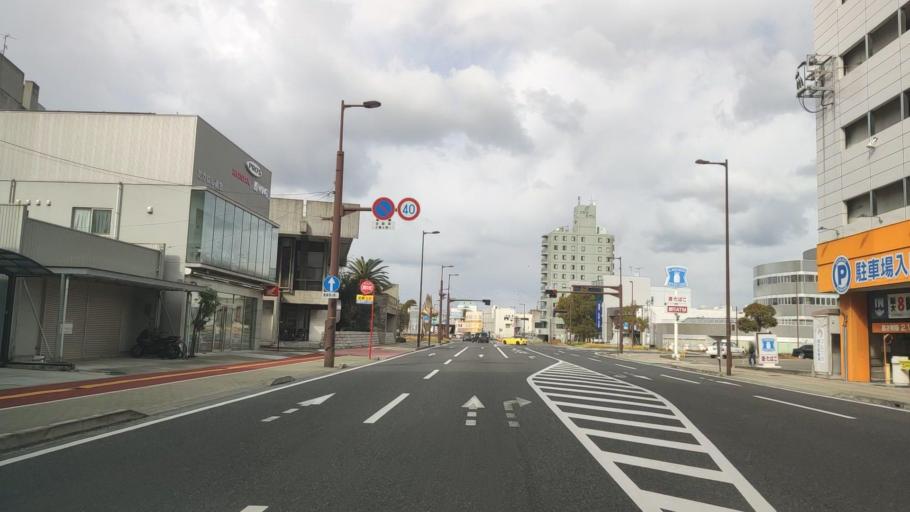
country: JP
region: Ehime
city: Saijo
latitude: 34.0659
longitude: 132.9989
